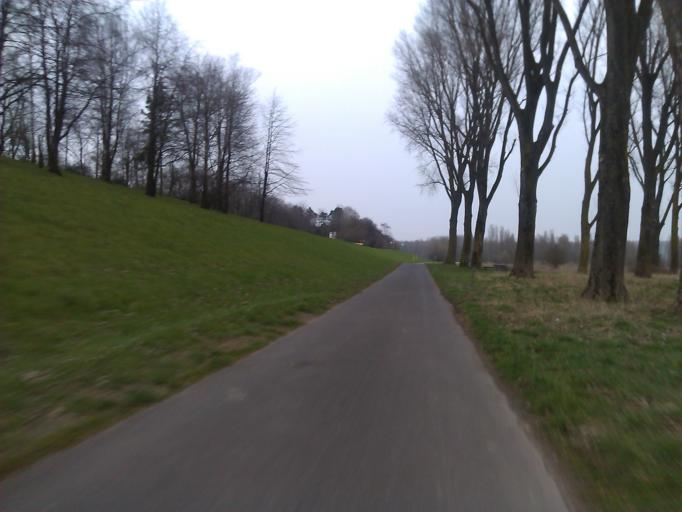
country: DE
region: North Rhine-Westphalia
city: Monheim am Rhein
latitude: 51.0987
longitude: 6.8663
